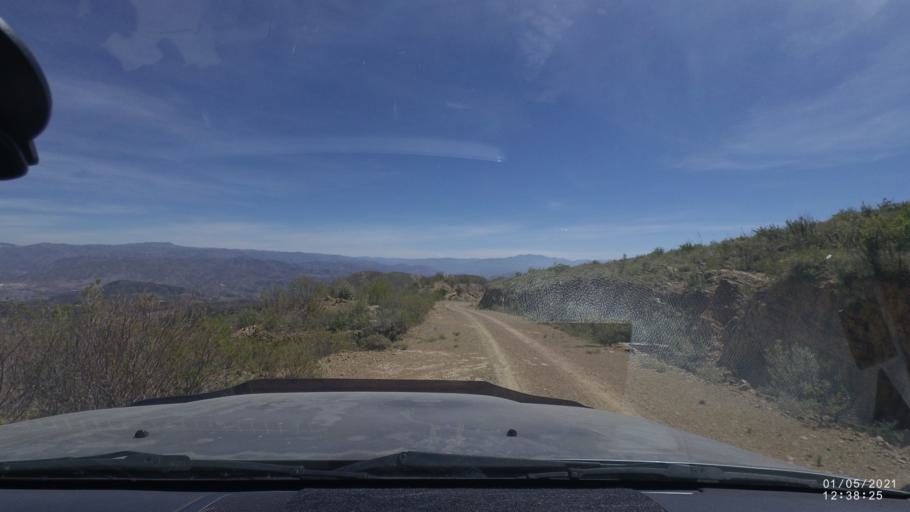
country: BO
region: Cochabamba
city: Capinota
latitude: -17.6807
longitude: -66.1591
